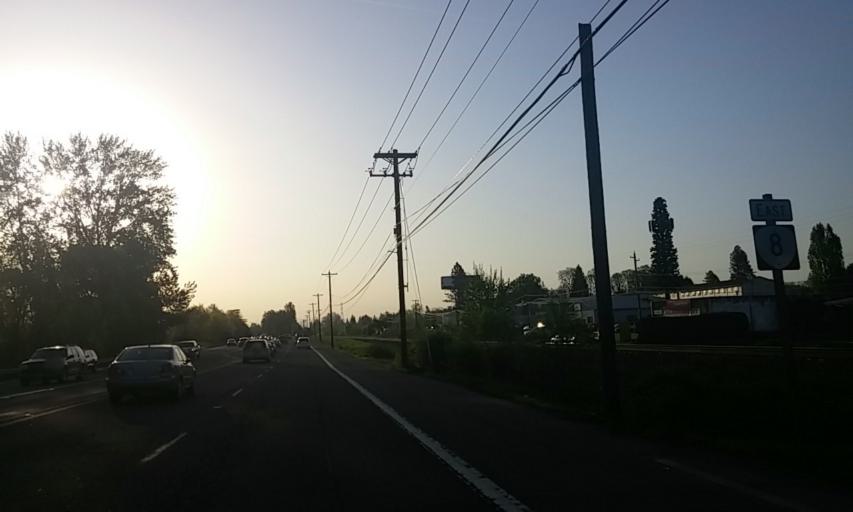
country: US
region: Oregon
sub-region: Washington County
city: Aloha
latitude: 45.4921
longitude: -122.8507
